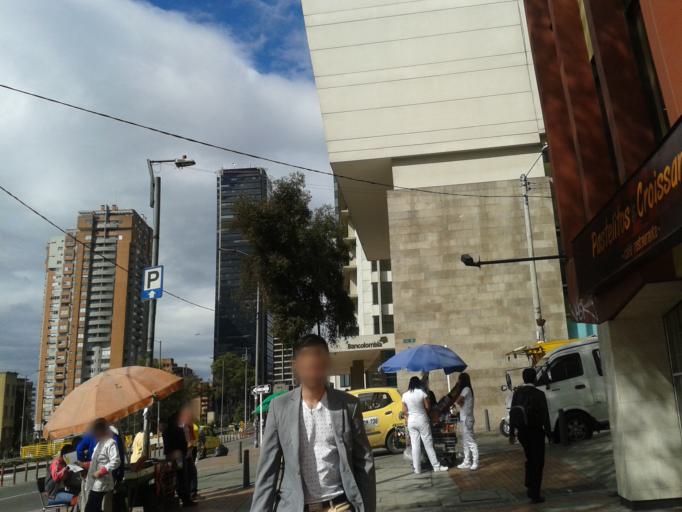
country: CO
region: Bogota D.C.
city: Bogota
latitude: 4.6158
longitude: -74.0687
